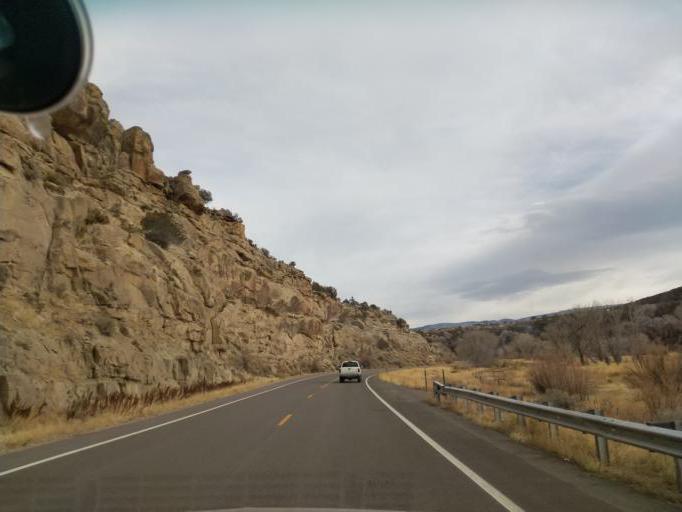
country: US
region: Colorado
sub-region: Mesa County
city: Palisade
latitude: 39.1896
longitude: -108.1584
